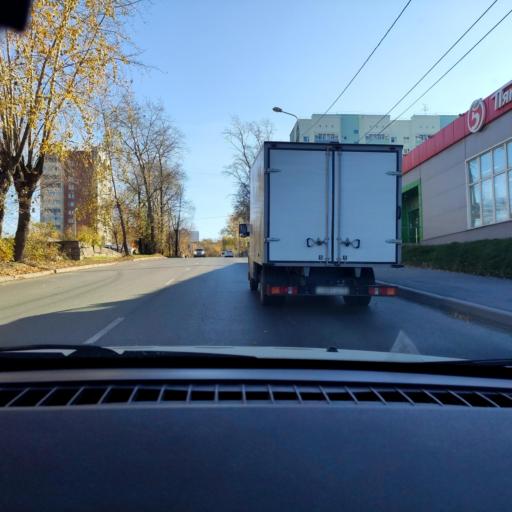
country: RU
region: Perm
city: Perm
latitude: 58.0689
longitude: 56.3548
